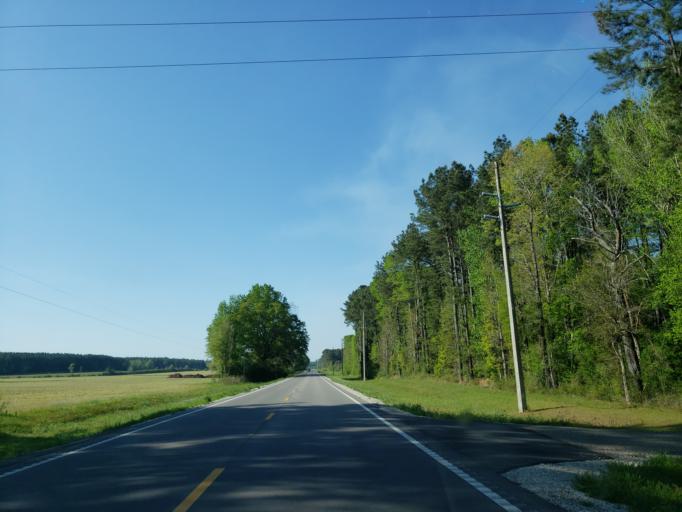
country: US
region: Mississippi
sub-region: Perry County
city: Richton
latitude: 31.3101
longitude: -88.9293
